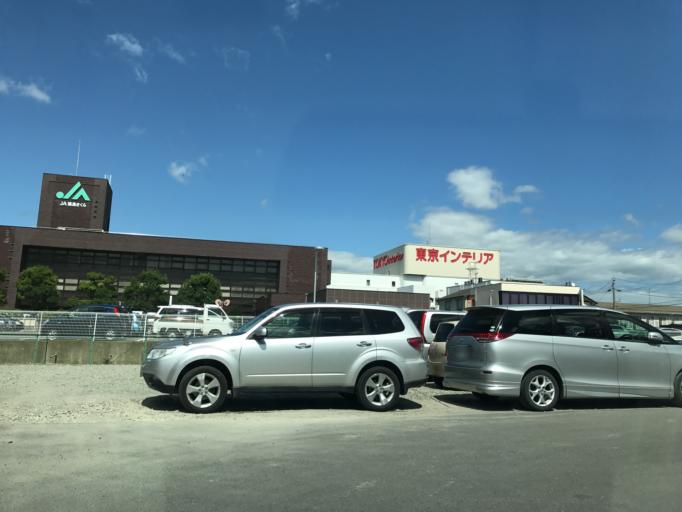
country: JP
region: Fukushima
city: Koriyama
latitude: 37.4047
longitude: 140.3604
